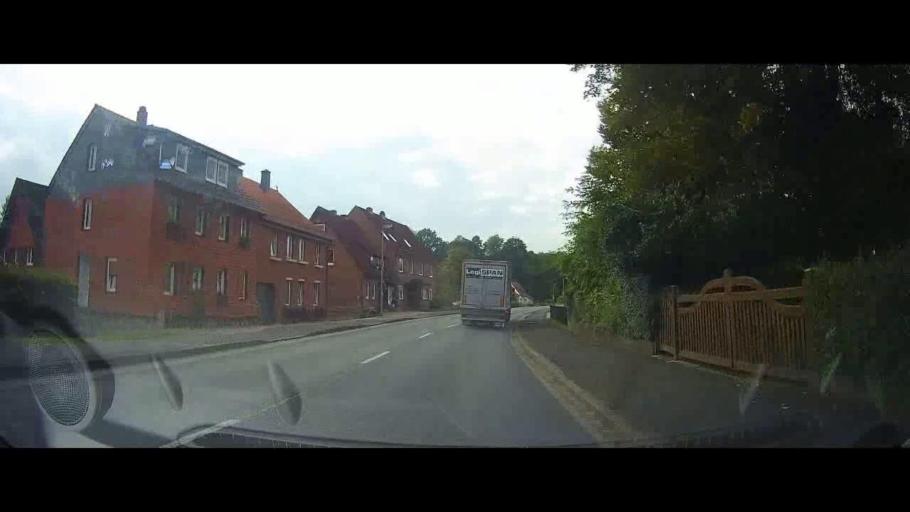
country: DE
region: Lower Saxony
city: Uslar
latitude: 51.6547
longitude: 9.6751
